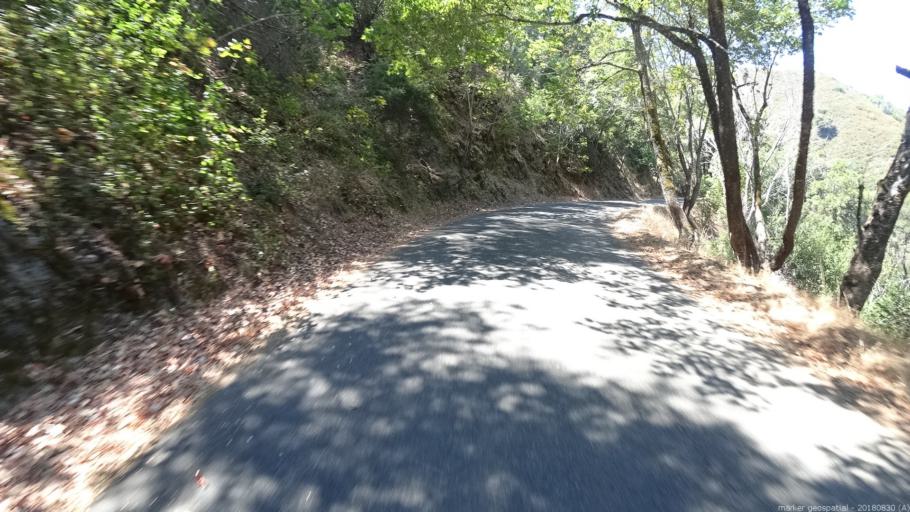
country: US
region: California
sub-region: Monterey County
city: Greenfield
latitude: 36.0100
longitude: -121.4353
